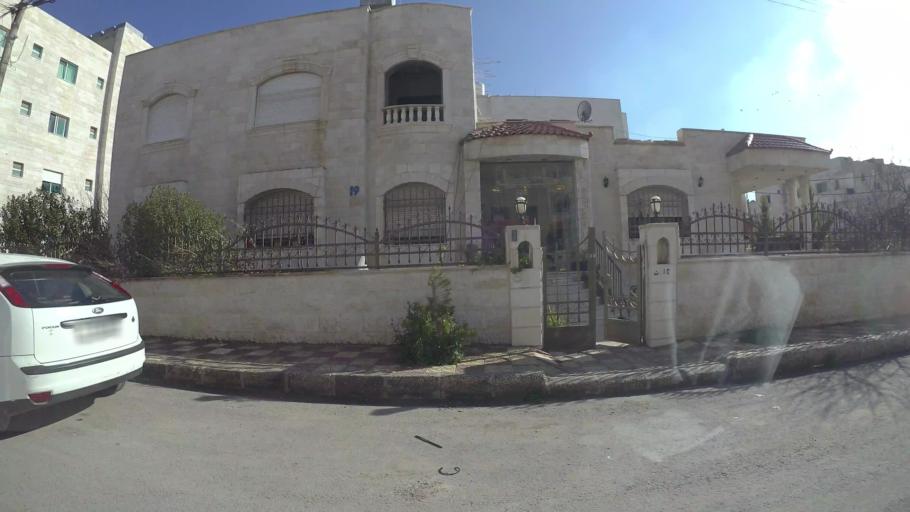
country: JO
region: Amman
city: Al Bunayyat ash Shamaliyah
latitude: 31.9023
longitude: 35.9163
